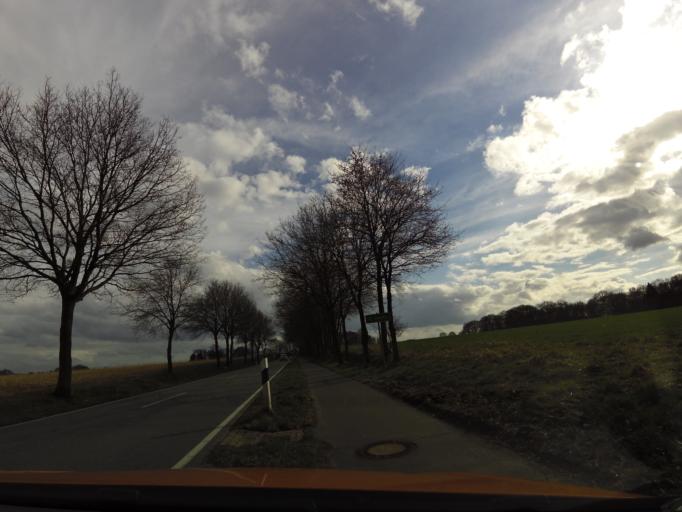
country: DE
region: Lower Saxony
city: Prinzhofte
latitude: 52.9274
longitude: 8.5682
